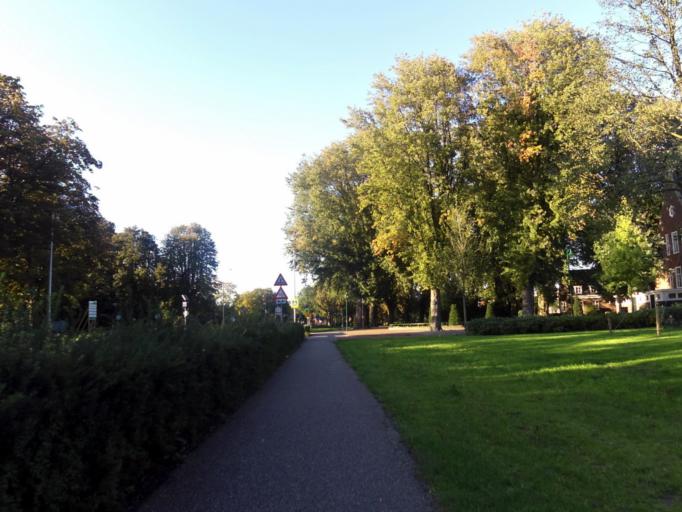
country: NL
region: South Holland
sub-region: Gemeente Alphen aan den Rijn
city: Alphen aan den Rijn
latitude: 52.1306
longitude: 4.6576
